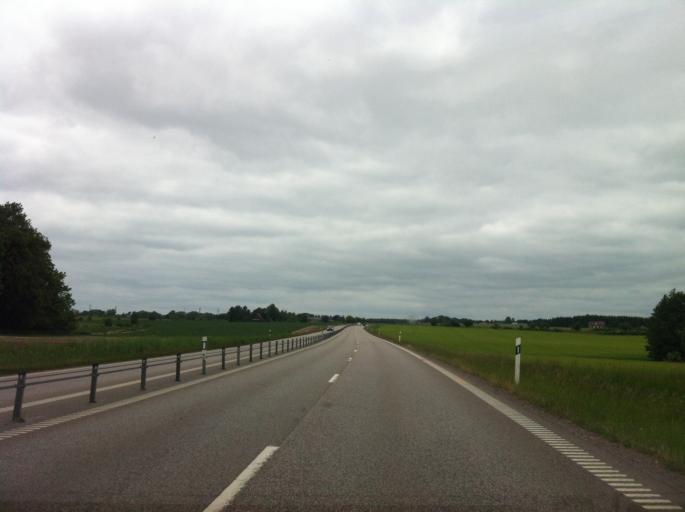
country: SE
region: Skane
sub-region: Hoors Kommun
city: Loberod
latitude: 55.7940
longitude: 13.4045
